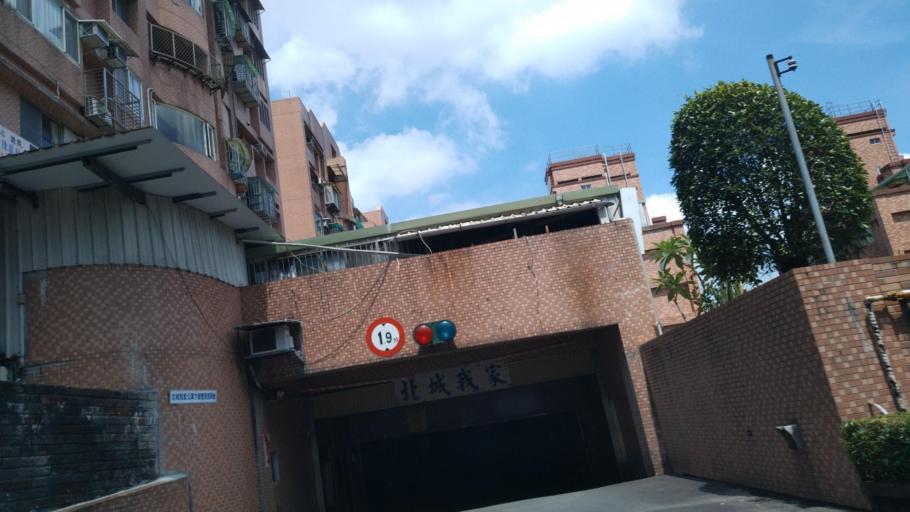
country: TW
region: Taipei
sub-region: Taipei
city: Banqiao
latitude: 24.9472
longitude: 121.4957
